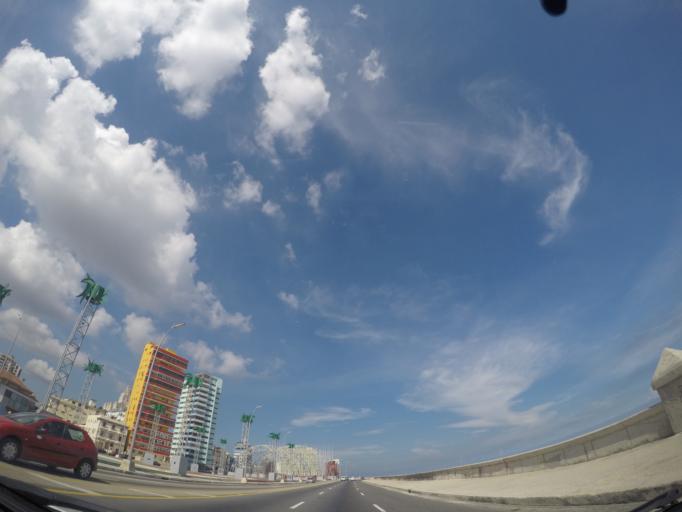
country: CU
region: La Habana
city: Havana
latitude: 23.1454
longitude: -82.3841
